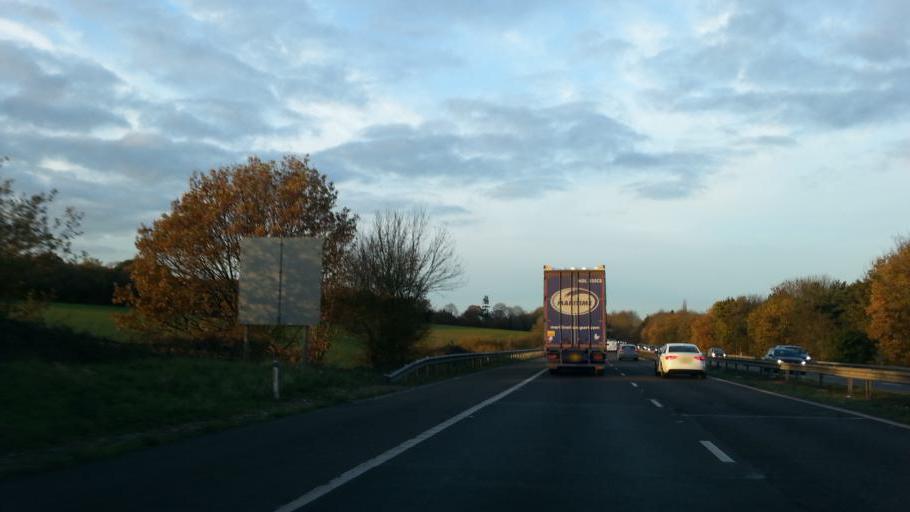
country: GB
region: England
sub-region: Hertfordshire
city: Knebworth
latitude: 51.8618
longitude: -0.1966
